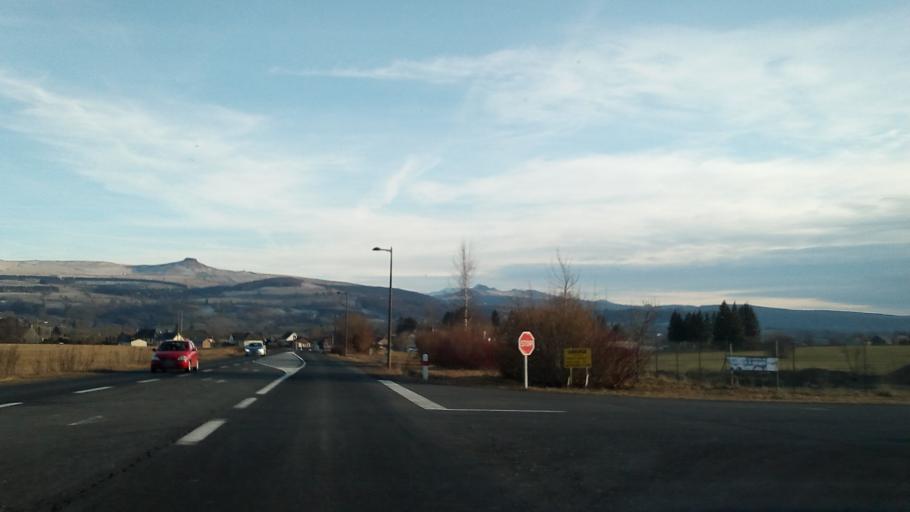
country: FR
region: Auvergne
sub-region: Departement du Puy-de-Dome
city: Saint-Sauves-d'Auvergne
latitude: 45.6514
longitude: 2.7022
